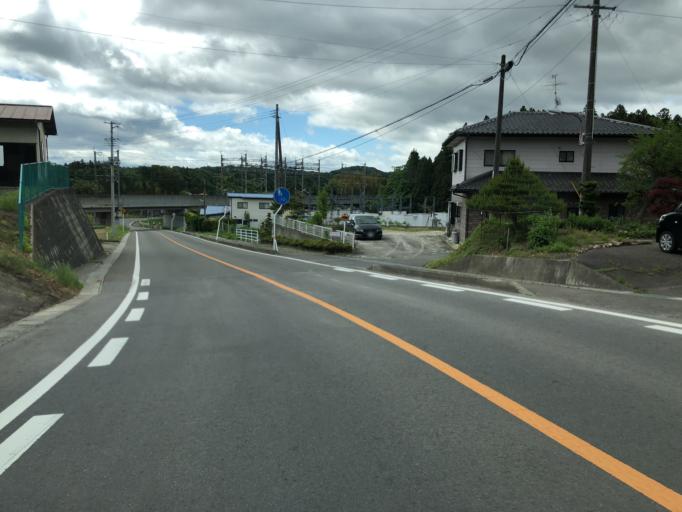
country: JP
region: Fukushima
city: Nihommatsu
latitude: 37.5624
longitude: 140.4555
